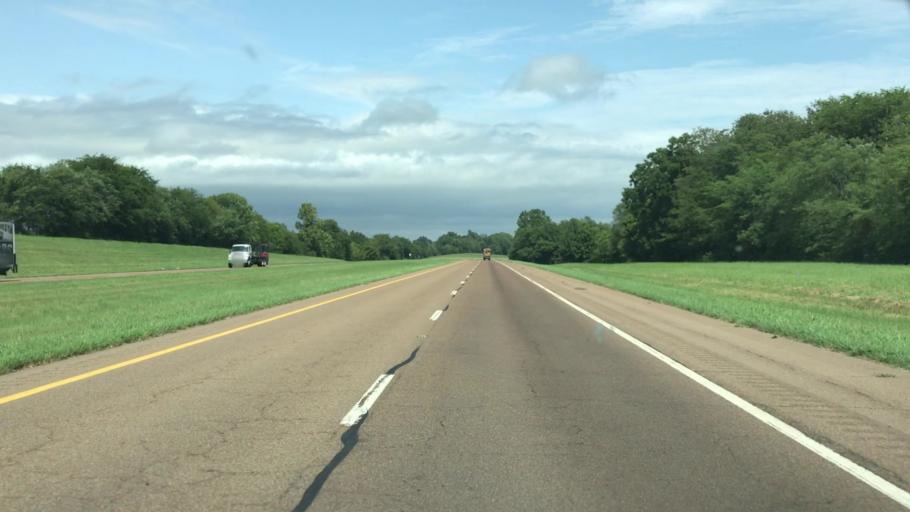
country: US
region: Tennessee
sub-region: Obion County
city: South Fulton
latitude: 36.4913
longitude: -88.9211
